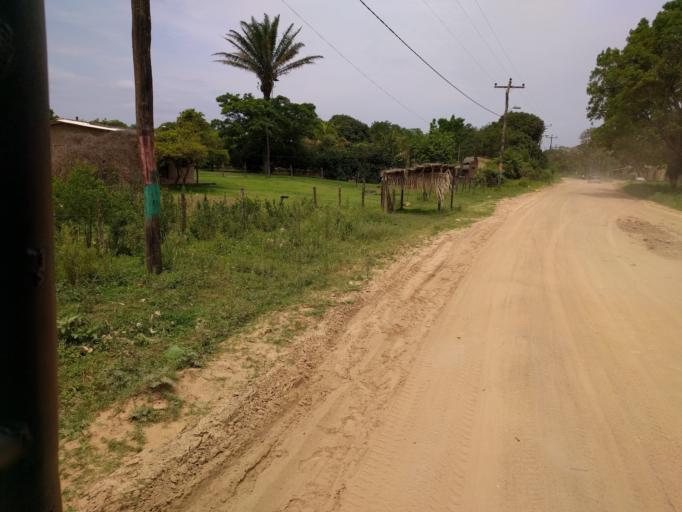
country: BO
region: Santa Cruz
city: Santa Rita
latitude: -17.9429
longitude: -63.3594
